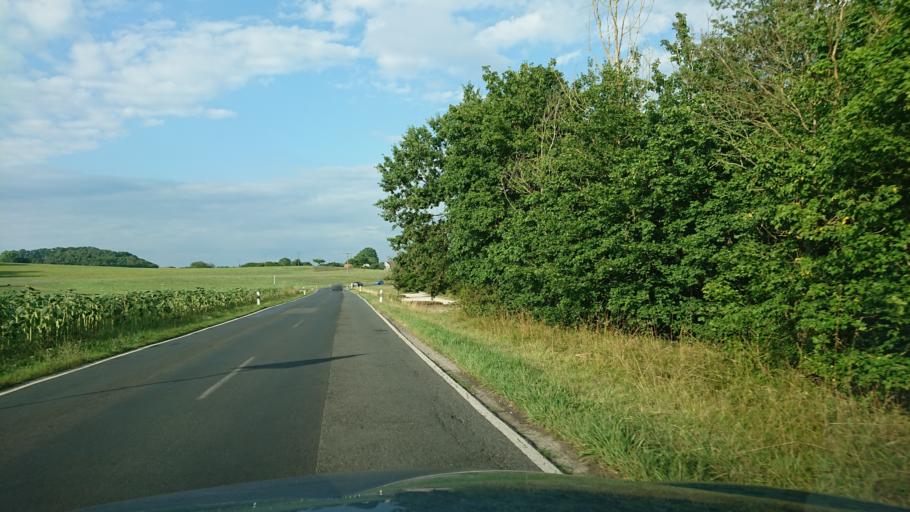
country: DE
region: Bavaria
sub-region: Regierungsbezirk Mittelfranken
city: Spardorf
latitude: 49.6053
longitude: 11.0479
